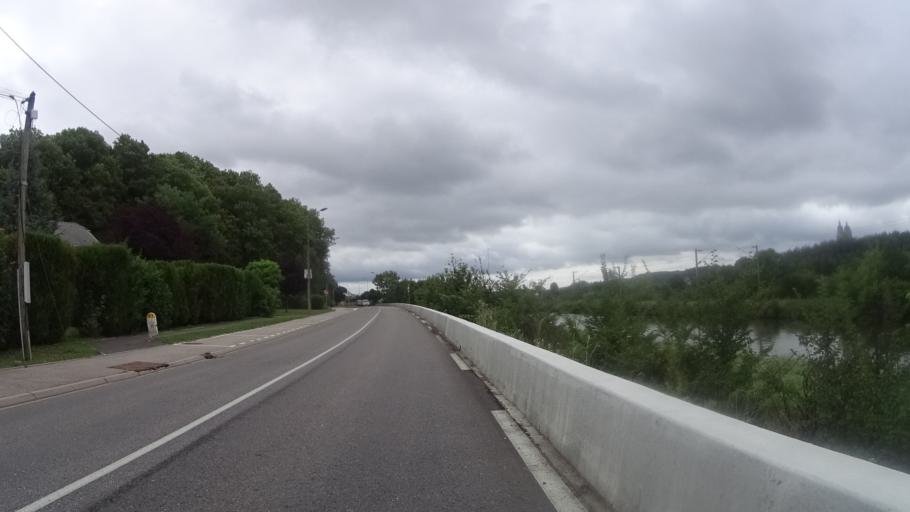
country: FR
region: Lorraine
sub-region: Departement de Meurthe-et-Moselle
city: Saint-Nicolas-de-Port
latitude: 48.6391
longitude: 6.3031
